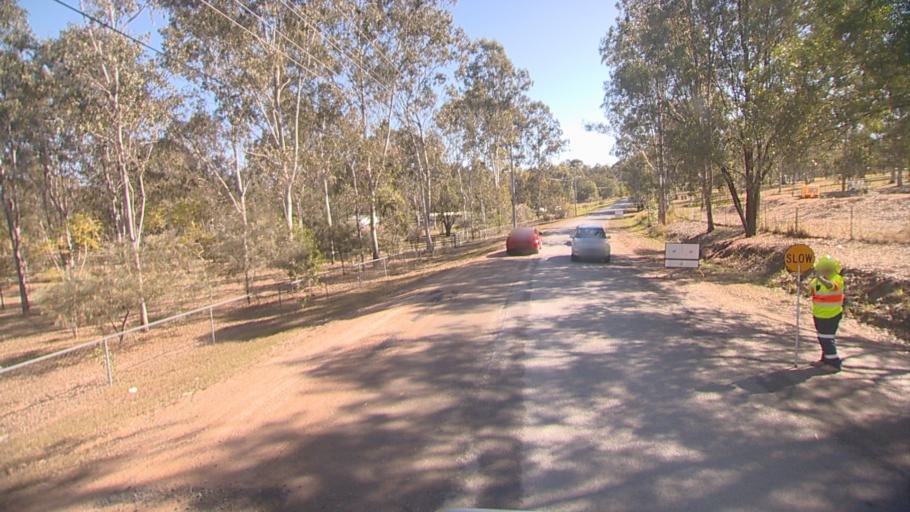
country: AU
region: Queensland
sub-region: Logan
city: Cedar Vale
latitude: -27.8576
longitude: 153.0193
